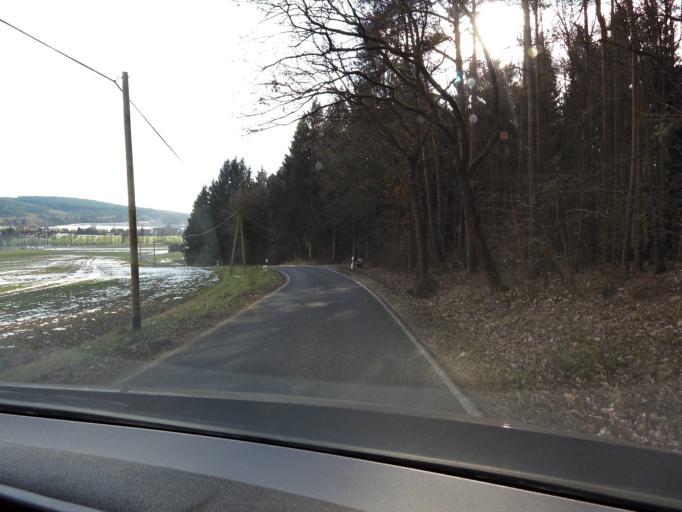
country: DE
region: Thuringia
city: Leimbach
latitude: 50.8544
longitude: 10.2124
